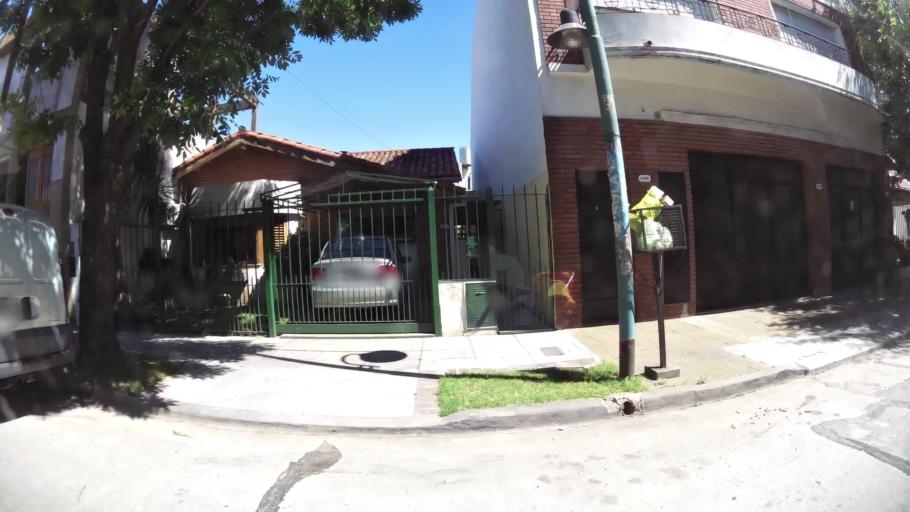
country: AR
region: Buenos Aires
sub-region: Partido de General San Martin
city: General San Martin
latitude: -34.5267
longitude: -58.5309
